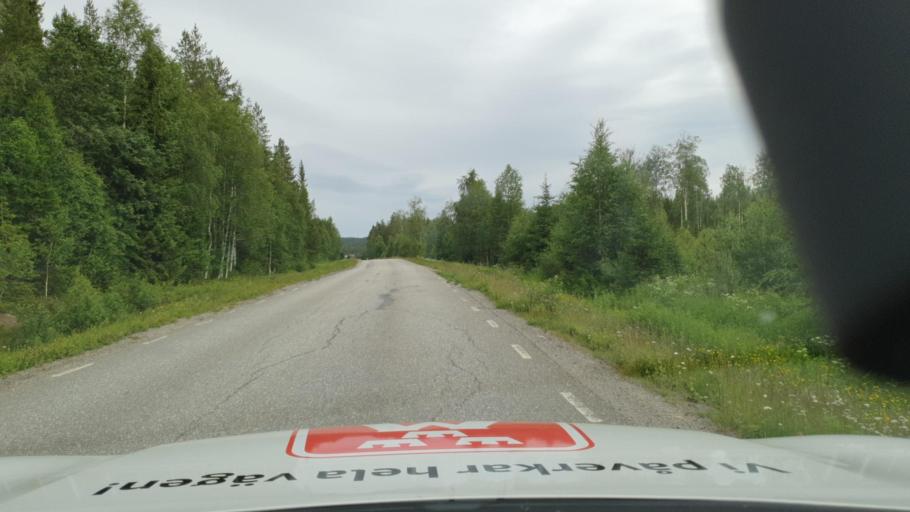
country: SE
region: Vaesterbotten
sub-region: Skelleftea Kommun
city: Burtraesk
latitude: 64.2982
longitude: 20.6474
